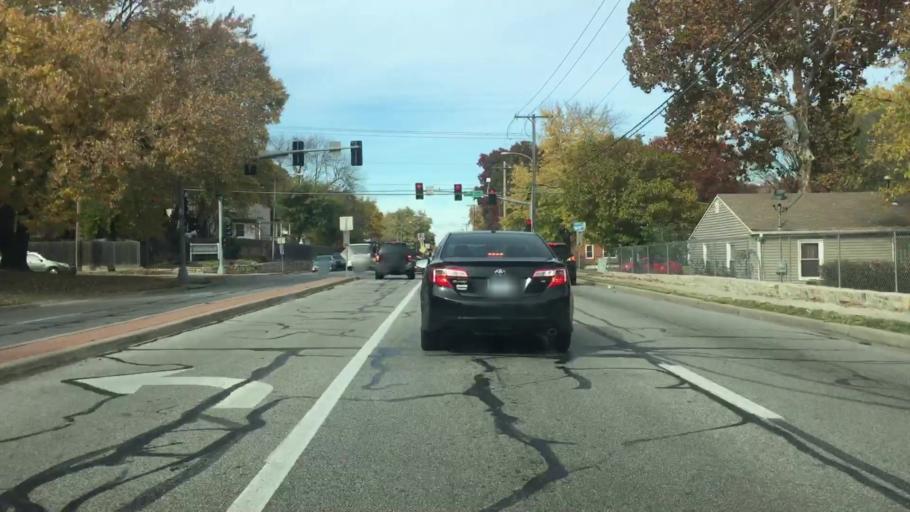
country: US
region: Kansas
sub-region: Johnson County
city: Merriam
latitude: 39.0069
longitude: -94.7237
